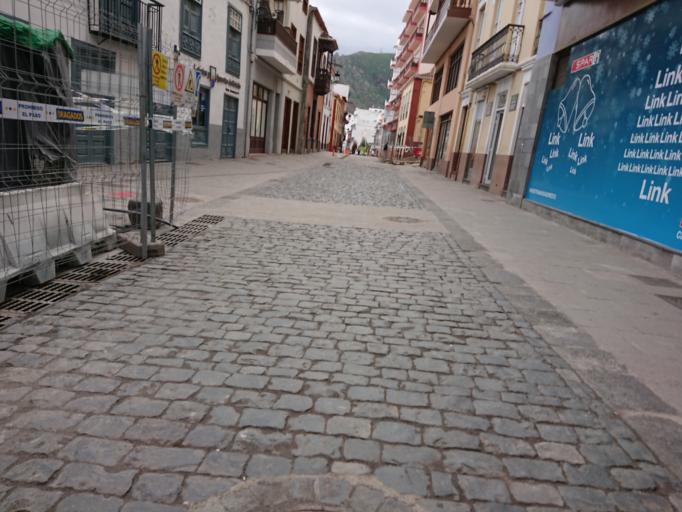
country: ES
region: Canary Islands
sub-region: Provincia de Santa Cruz de Tenerife
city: Santa Cruz de la Palma
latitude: 28.6866
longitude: -17.7616
